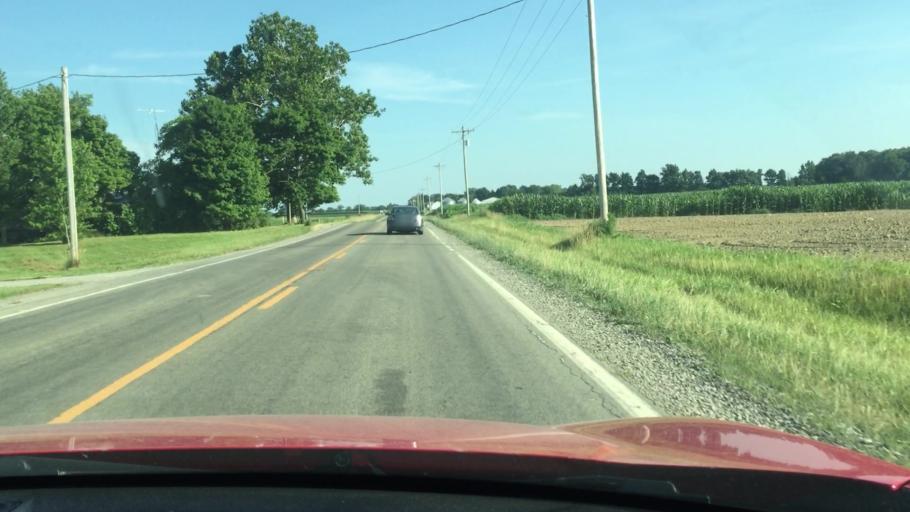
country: US
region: Ohio
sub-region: Hardin County
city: Ada
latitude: 40.6642
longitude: -83.8526
